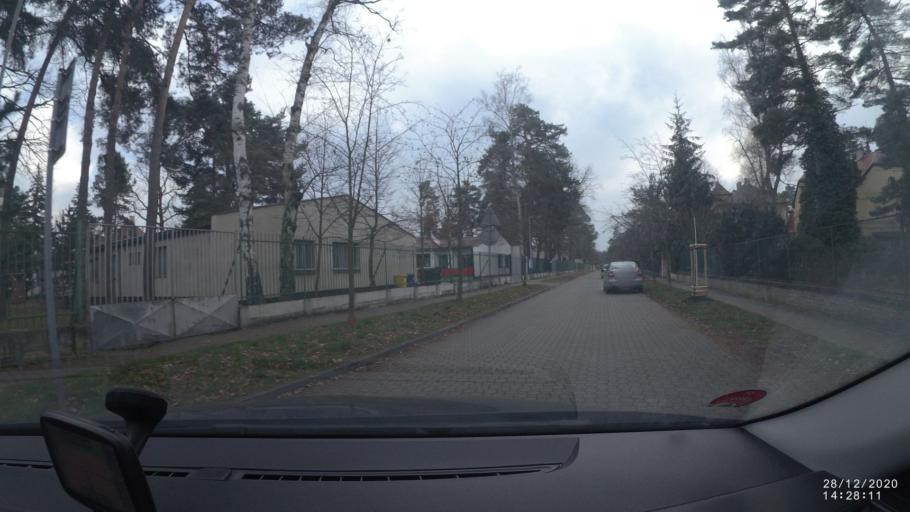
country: CZ
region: Central Bohemia
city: Sestajovice
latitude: 50.0921
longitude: 14.6653
